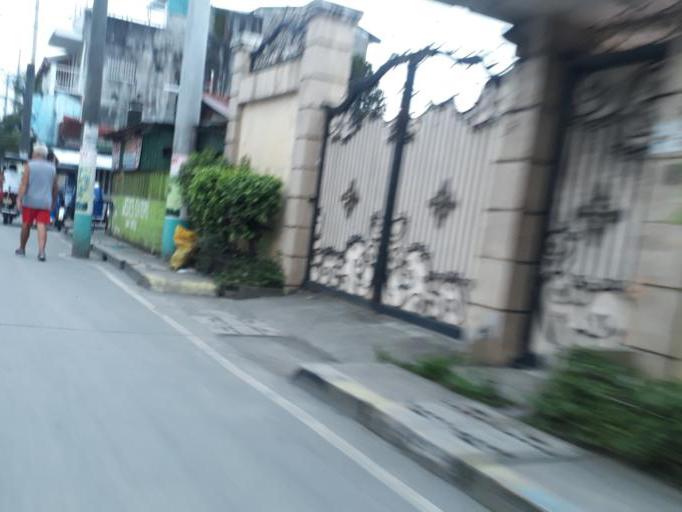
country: PH
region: Calabarzon
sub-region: Province of Rizal
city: Valenzuela
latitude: 14.7062
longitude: 120.9536
